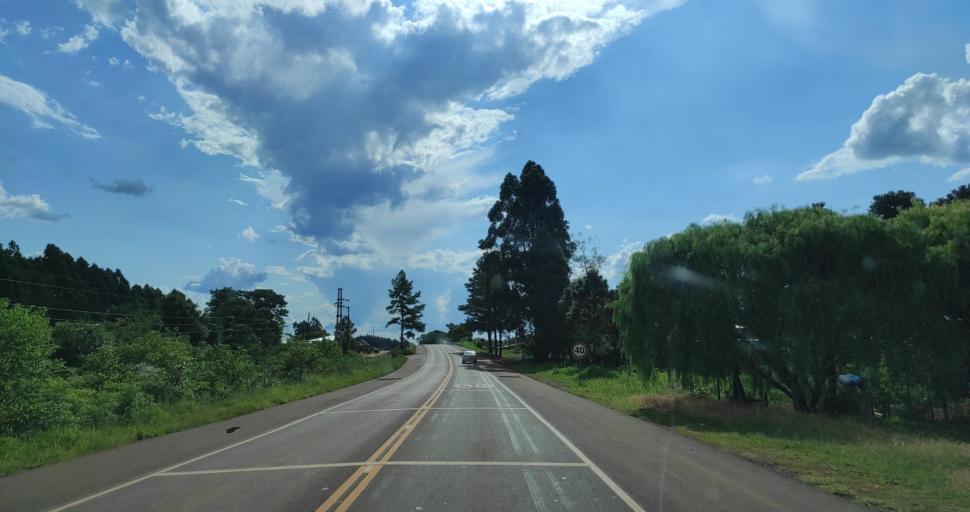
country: AR
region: Misiones
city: Bernardo de Irigoyen
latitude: -26.2954
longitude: -53.7872
